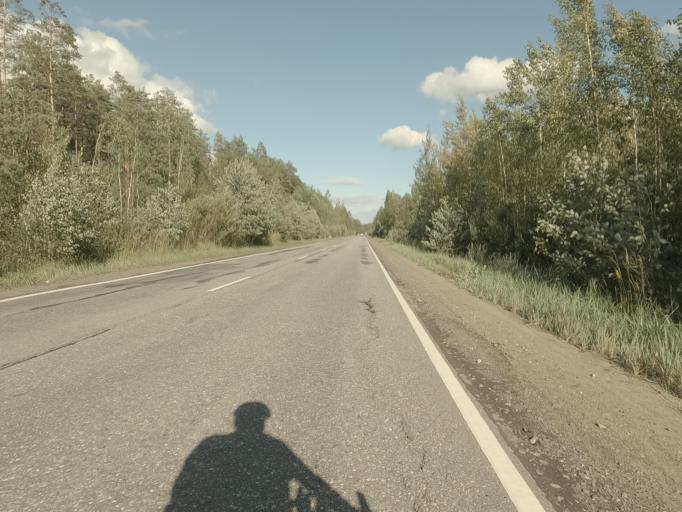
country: RU
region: Leningrad
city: Borisova Griva
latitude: 59.9853
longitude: 30.9114
